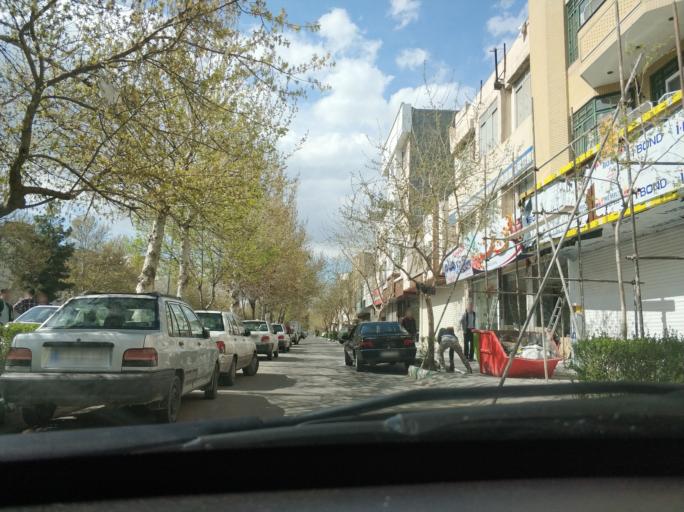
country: IR
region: Razavi Khorasan
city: Mashhad
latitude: 36.2701
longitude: 59.5968
